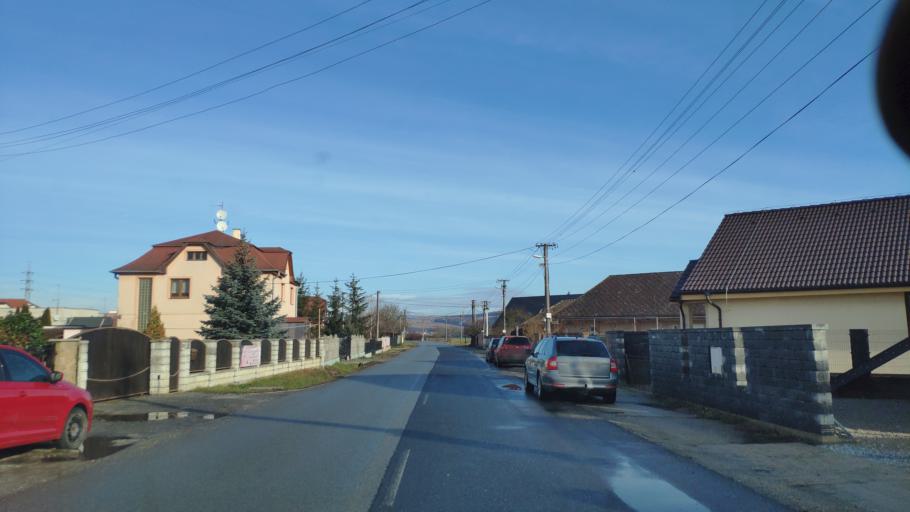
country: SK
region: Kosicky
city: Kosice
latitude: 48.6737
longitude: 21.3212
